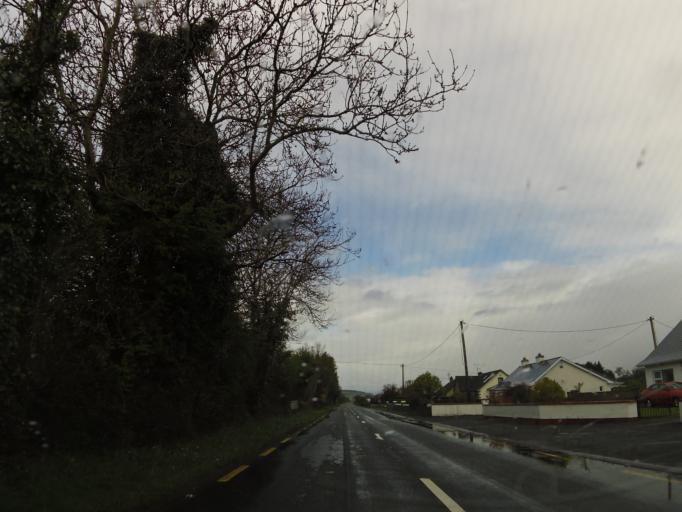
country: IE
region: Connaught
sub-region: Sligo
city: Collooney
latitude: 54.1980
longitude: -8.4968
